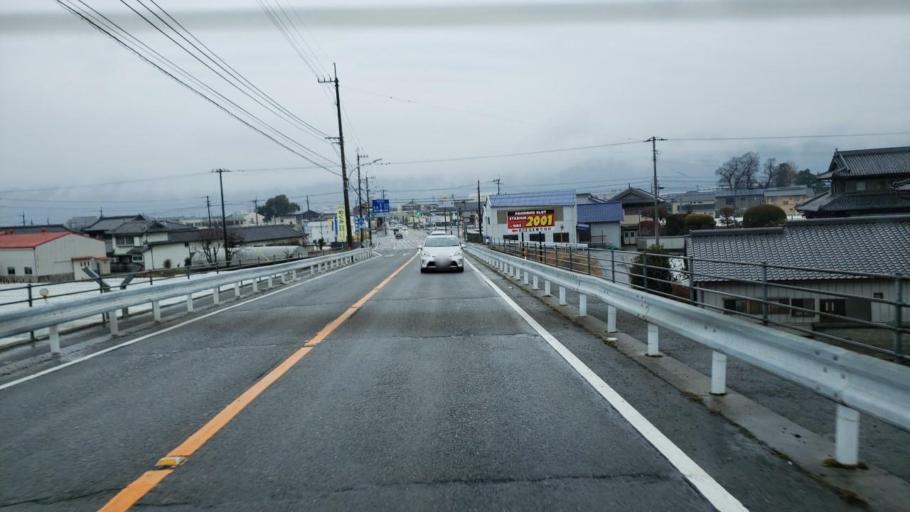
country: JP
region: Tokushima
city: Kamojimacho-jogejima
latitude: 34.0821
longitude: 134.3480
